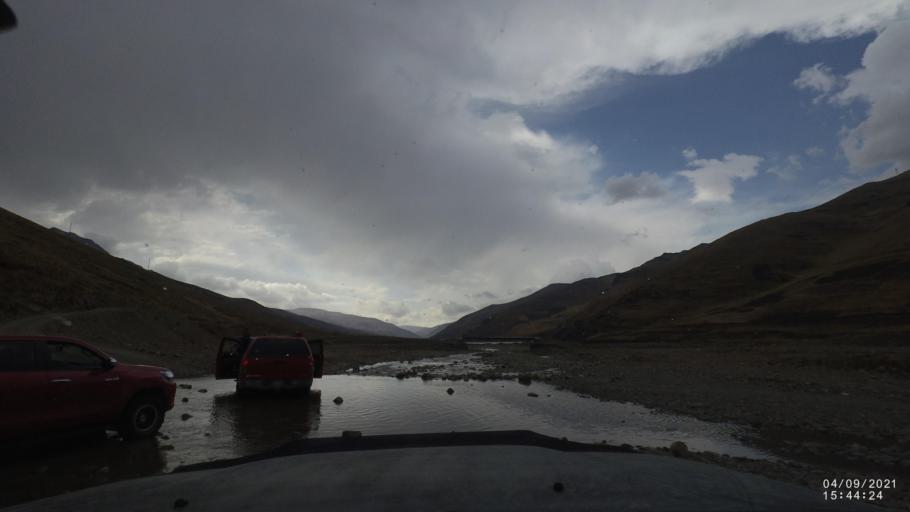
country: BO
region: Cochabamba
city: Cochabamba
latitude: -17.1534
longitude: -66.3120
